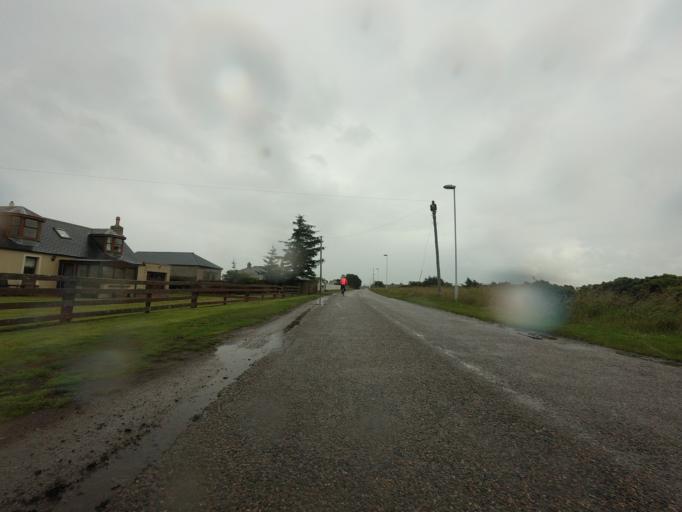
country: GB
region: Scotland
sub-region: Moray
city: Fochabers
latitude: 57.6731
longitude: -3.0892
